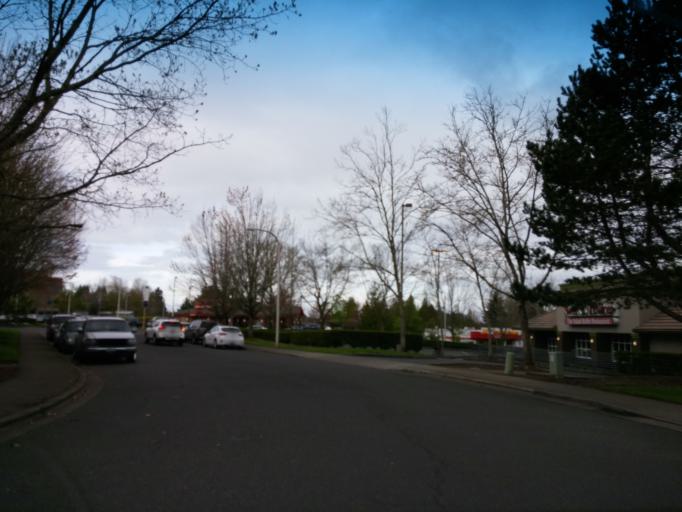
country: US
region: Oregon
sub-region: Washington County
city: Oak Hills
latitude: 45.5280
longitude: -122.8374
